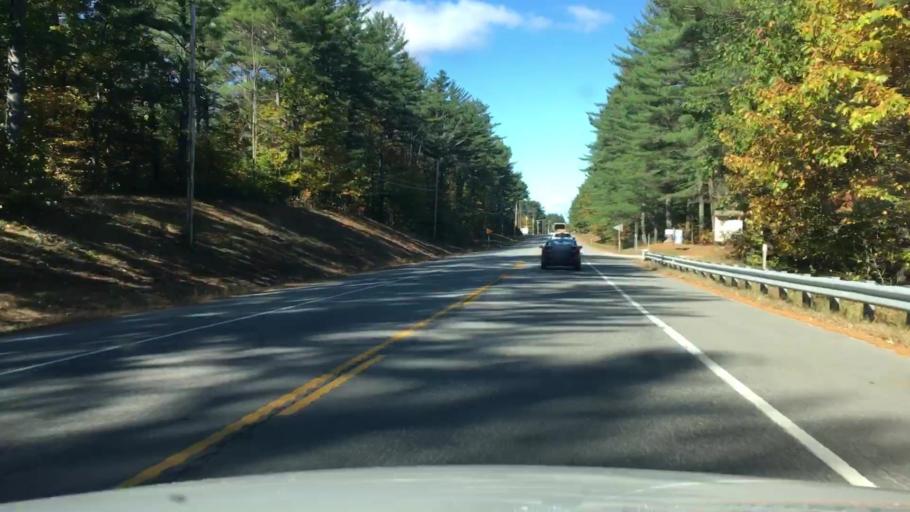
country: US
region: New Hampshire
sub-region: Carroll County
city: Ossipee
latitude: 43.6876
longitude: -71.0926
